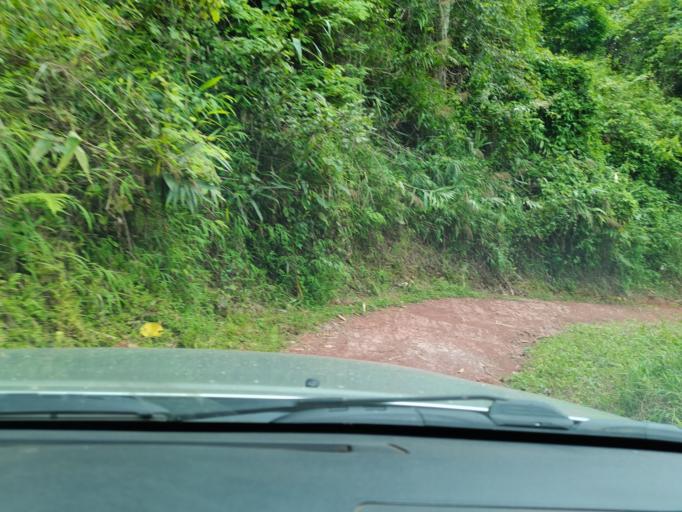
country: LA
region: Loungnamtha
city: Muang Nale
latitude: 20.5129
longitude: 101.0785
